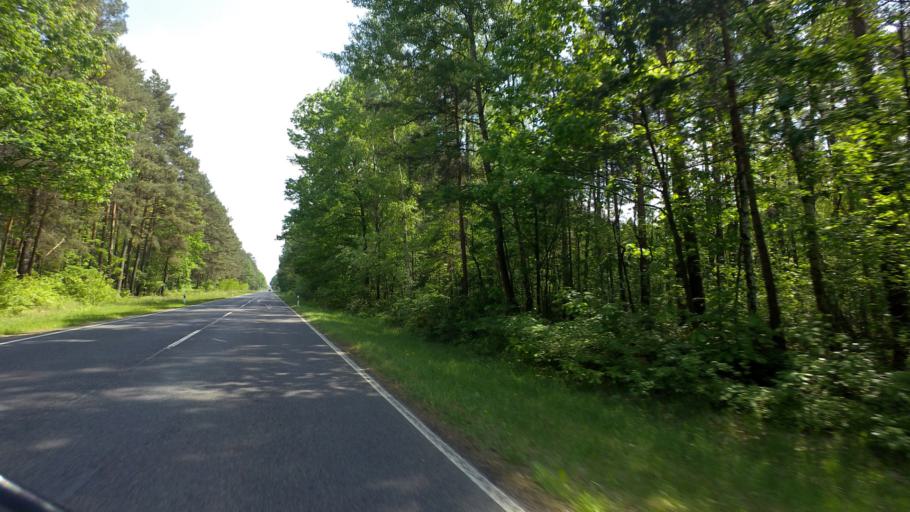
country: DE
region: Saxony
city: Schleife
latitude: 51.5510
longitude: 14.5112
